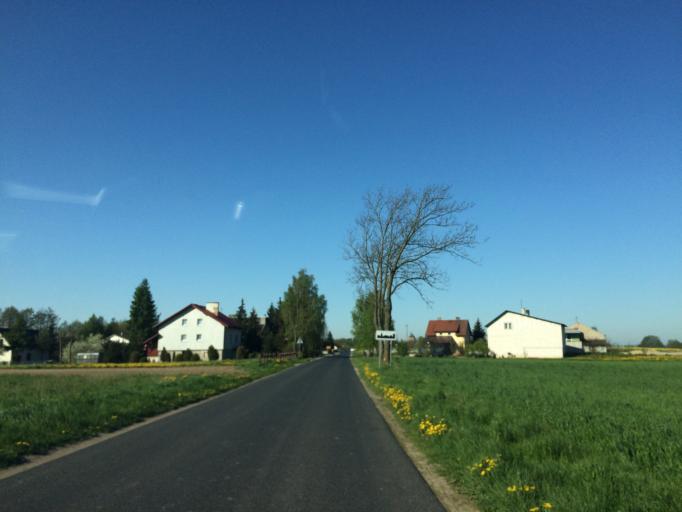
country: PL
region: Warmian-Masurian Voivodeship
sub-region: Powiat ilawski
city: Lubawa
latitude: 53.4177
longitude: 19.7699
